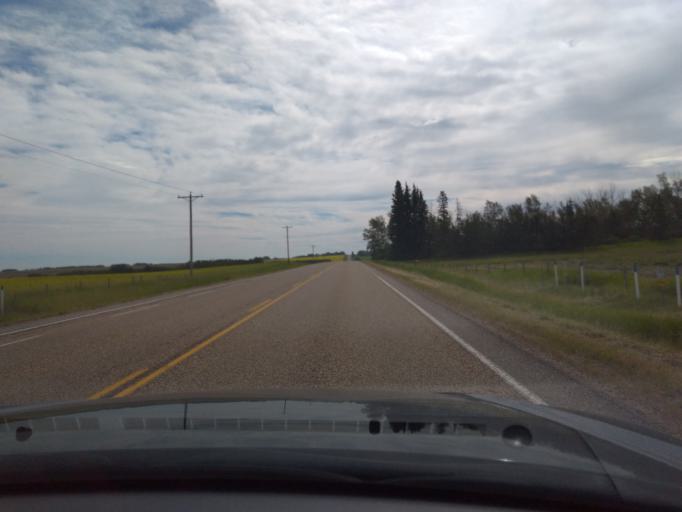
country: CA
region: Alberta
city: Carstairs
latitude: 51.5329
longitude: -114.1968
